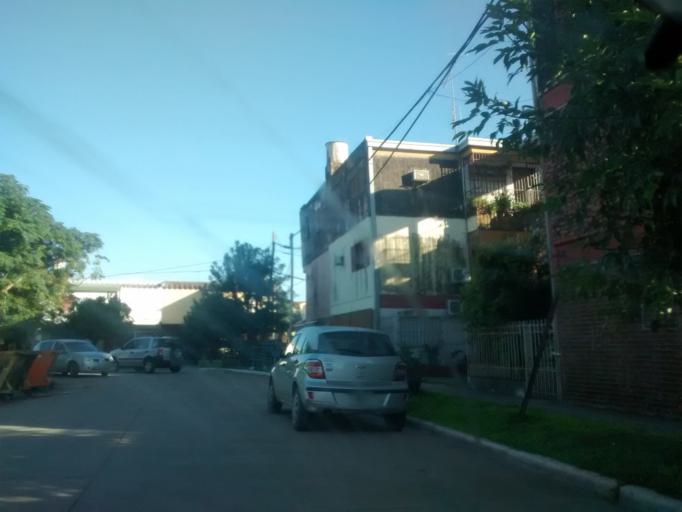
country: AR
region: Chaco
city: Fontana
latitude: -27.4462
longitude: -59.0156
